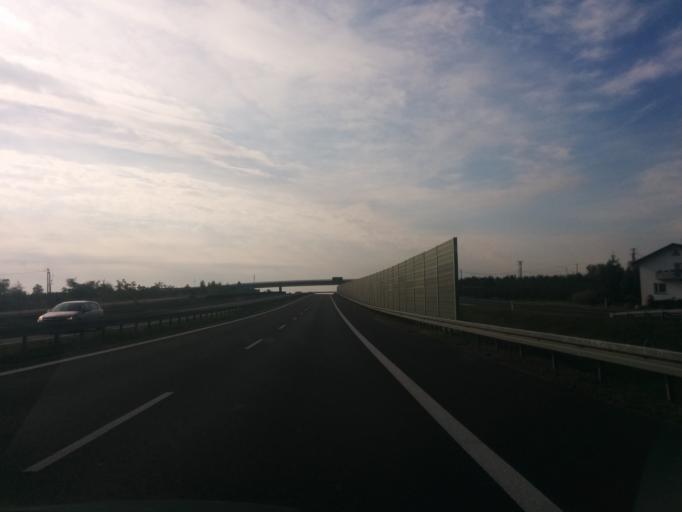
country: PL
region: Masovian Voivodeship
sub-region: Powiat grojecki
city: Jasieniec
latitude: 51.7894
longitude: 20.8928
